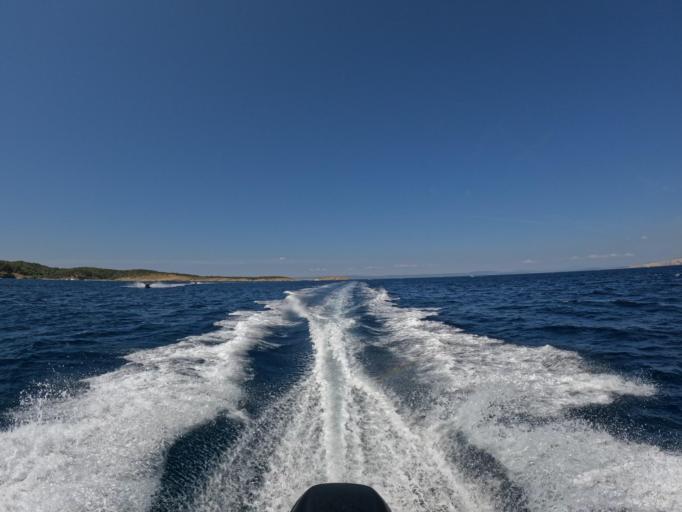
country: HR
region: Primorsko-Goranska
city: Lopar
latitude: 44.8528
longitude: 14.7428
